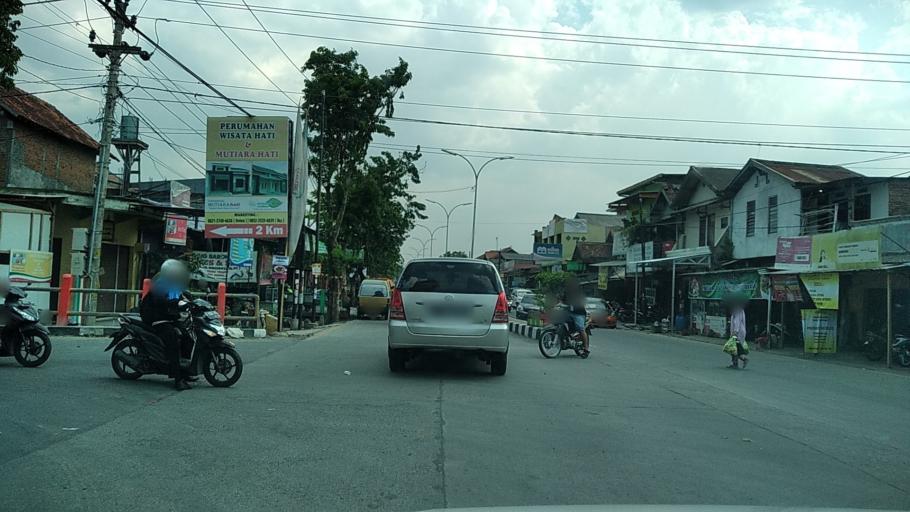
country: ID
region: Central Java
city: Semarang
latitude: -6.9530
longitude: 110.4806
